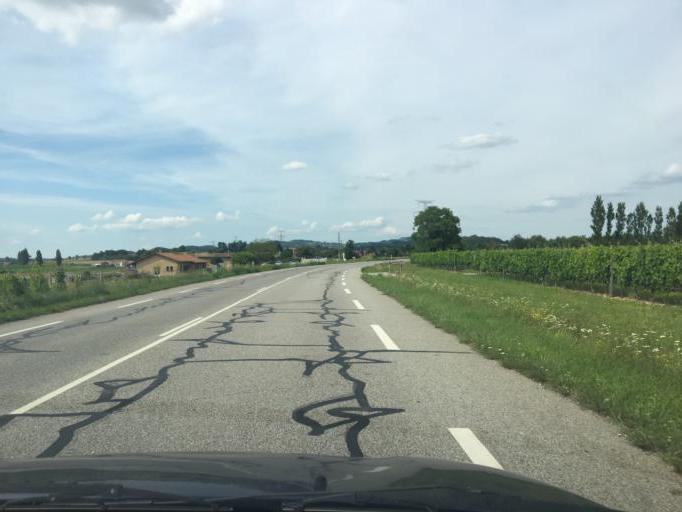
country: FR
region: Rhone-Alpes
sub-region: Departement de la Drome
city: Clerieux
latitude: 45.0918
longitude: 4.9366
